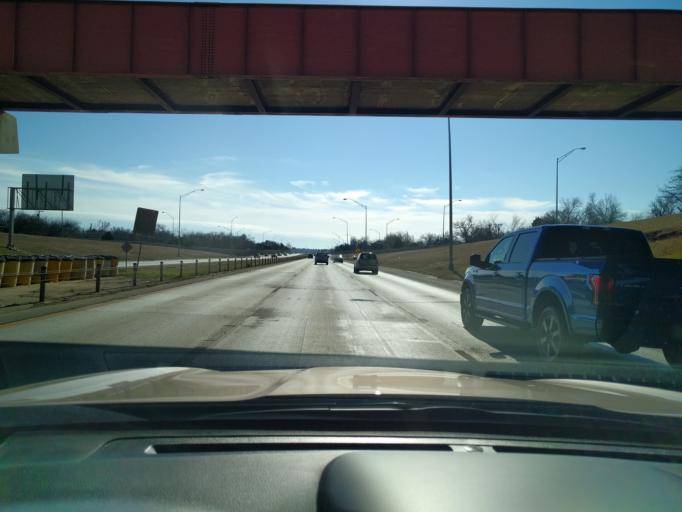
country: US
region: Oklahoma
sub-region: Oklahoma County
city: Nichols Hills
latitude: 35.5223
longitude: -97.5768
